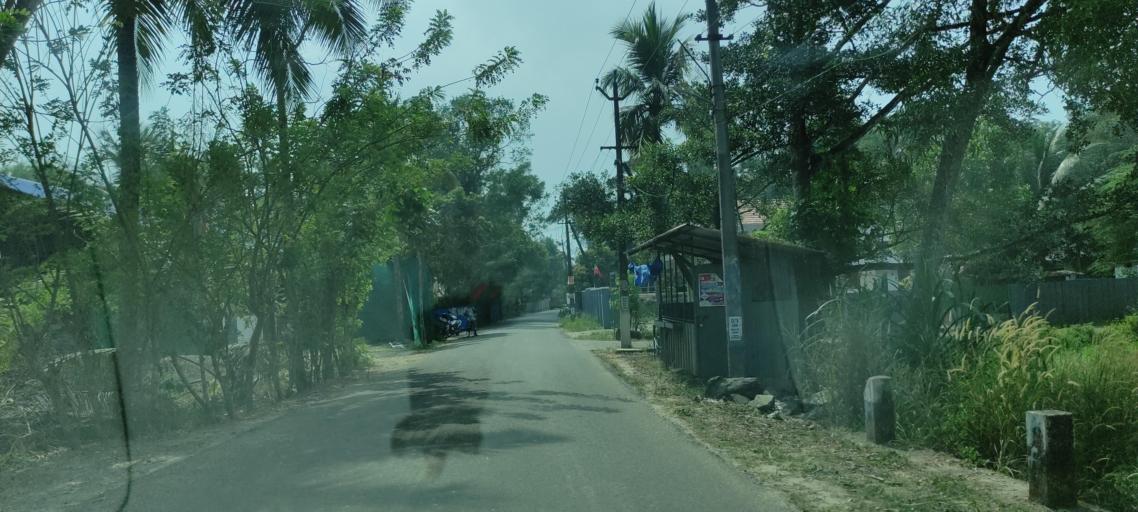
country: IN
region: Kerala
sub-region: Alappuzha
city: Shertallai
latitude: 9.6206
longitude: 76.3487
